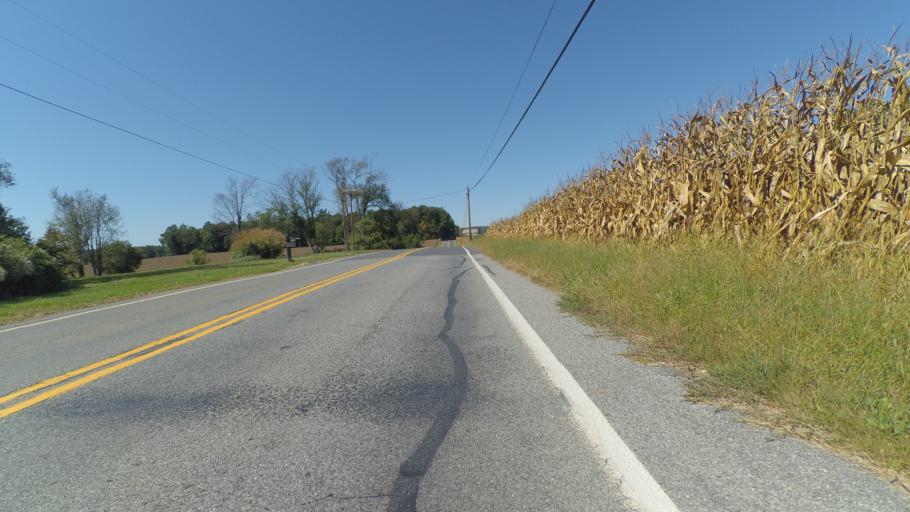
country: US
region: Pennsylvania
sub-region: Centre County
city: Pine Grove Mills
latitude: 40.7603
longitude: -77.9088
